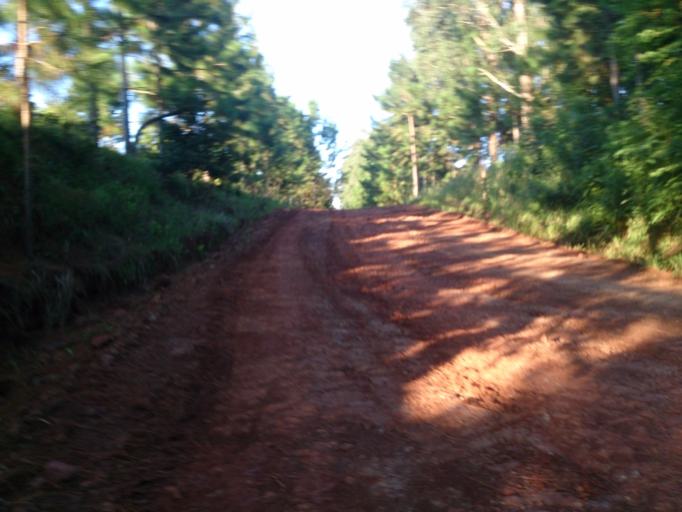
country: AR
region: Misiones
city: Florentino Ameghino
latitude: -27.5630
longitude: -55.1640
